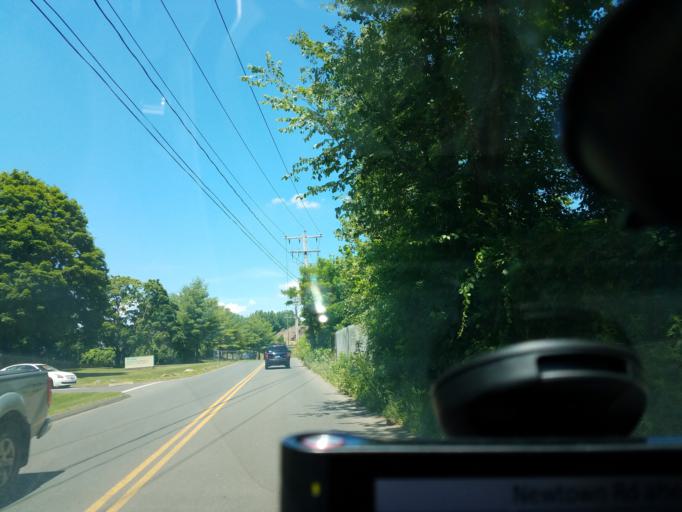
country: US
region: Connecticut
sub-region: Fairfield County
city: Bethel
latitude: 41.4007
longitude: -73.4150
